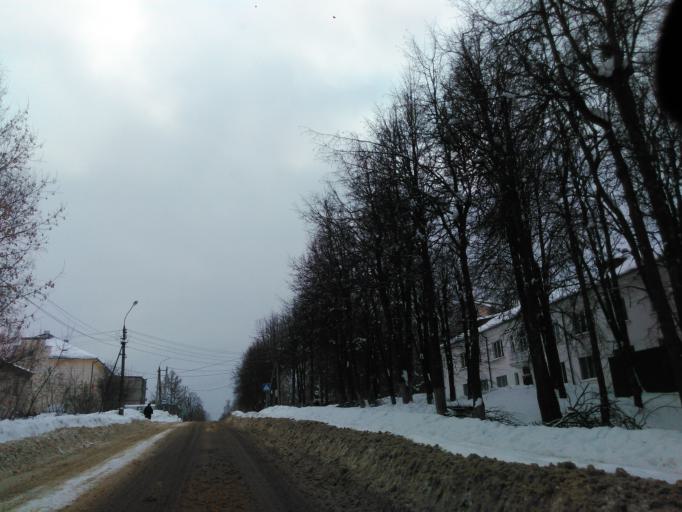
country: RU
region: Moskovskaya
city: Yakhroma
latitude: 56.2795
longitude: 37.4836
